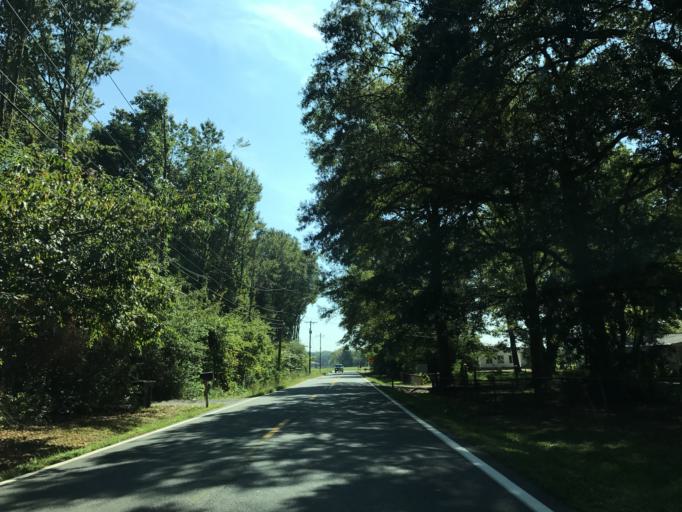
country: US
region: Maryland
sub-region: Cecil County
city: Elkton
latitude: 39.5128
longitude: -75.8127
